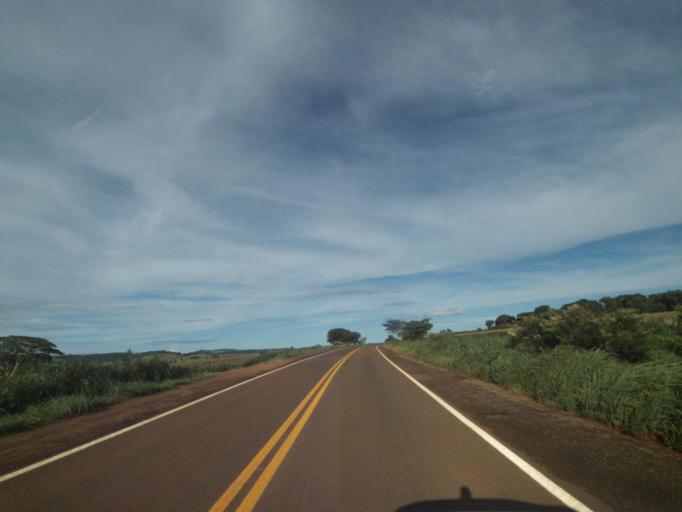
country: BR
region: Goias
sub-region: Jaragua
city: Jaragua
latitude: -15.9065
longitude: -49.5532
